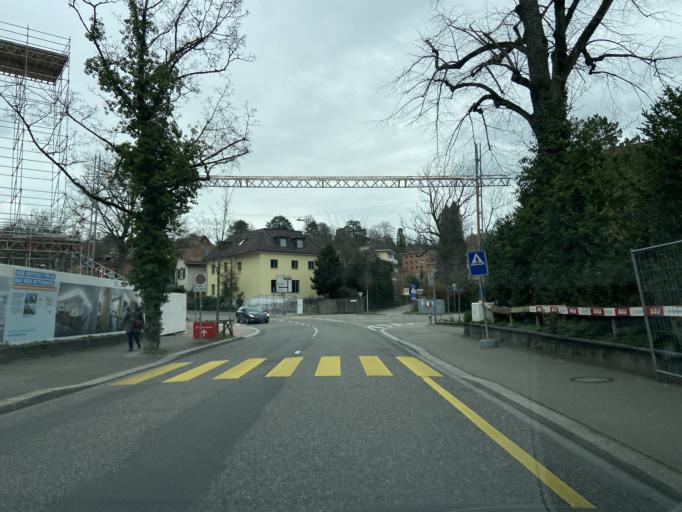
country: CH
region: Zurich
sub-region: Bezirk Winterthur
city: Stadt Winterthur (Kreis 1) / Lind
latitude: 47.5059
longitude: 8.7297
